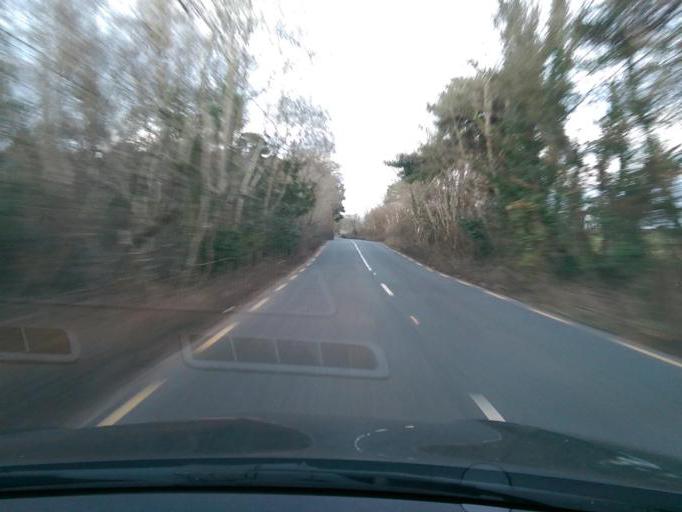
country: IE
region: Connaught
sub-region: County Galway
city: Portumna
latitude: 53.0684
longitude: -8.0856
